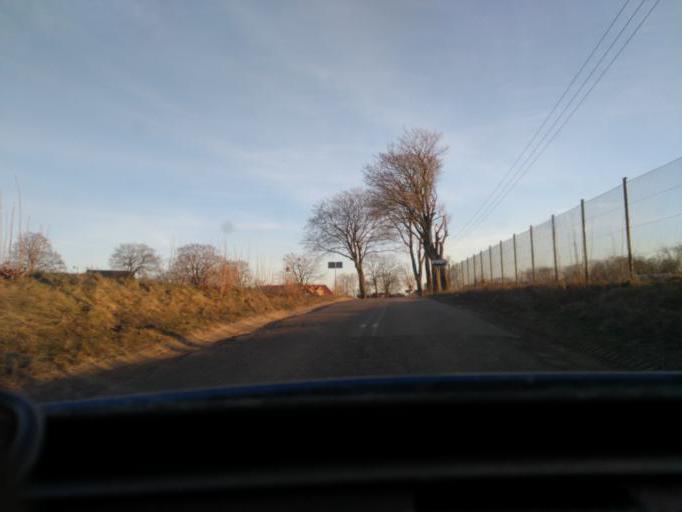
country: PL
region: Pomeranian Voivodeship
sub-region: Powiat kartuski
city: Przodkowo
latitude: 54.4035
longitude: 18.3305
